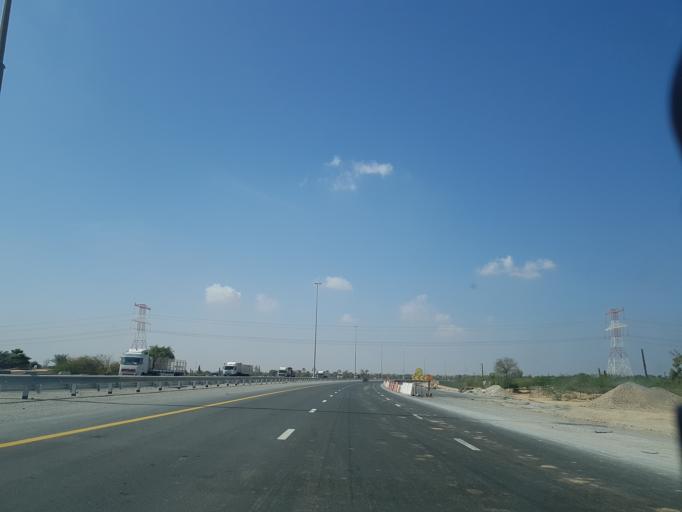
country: AE
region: Ra's al Khaymah
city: Ras al-Khaimah
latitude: 25.6979
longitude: 55.9842
